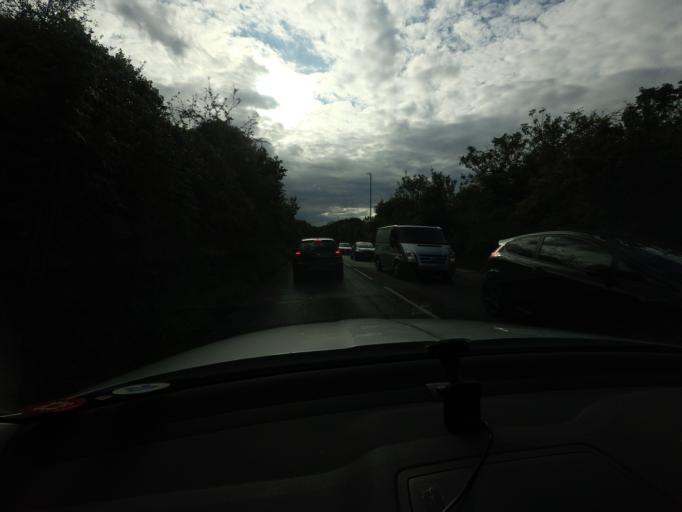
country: GB
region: England
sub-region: Kent
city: Greenhithe
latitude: 51.4497
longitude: 0.2839
